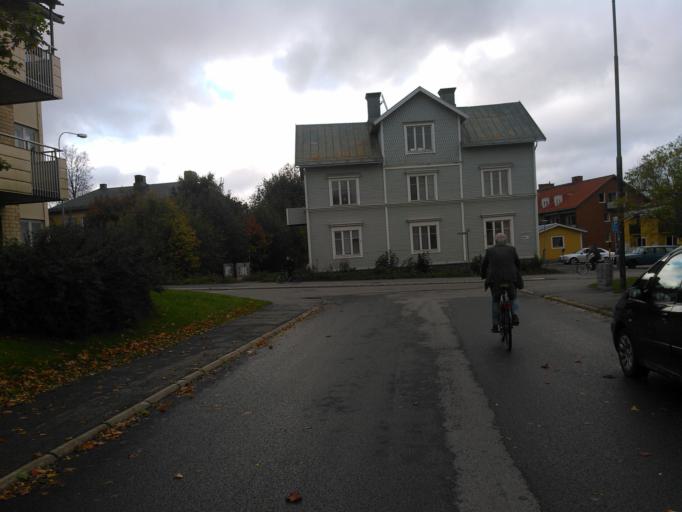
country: SE
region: Vaesterbotten
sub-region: Umea Kommun
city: Umea
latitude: 63.8225
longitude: 20.2482
